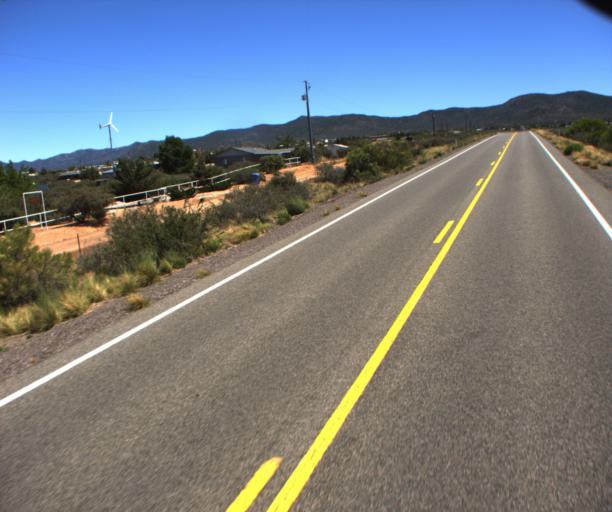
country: US
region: Arizona
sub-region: Yavapai County
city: Prescott
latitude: 34.4123
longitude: -112.6073
